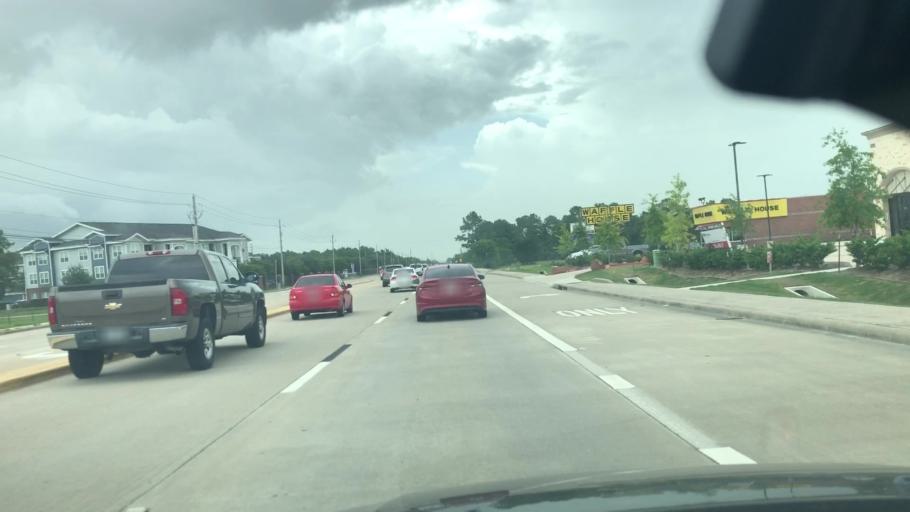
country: US
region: Texas
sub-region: Galveston County
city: Dickinson
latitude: 29.4741
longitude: -95.0788
